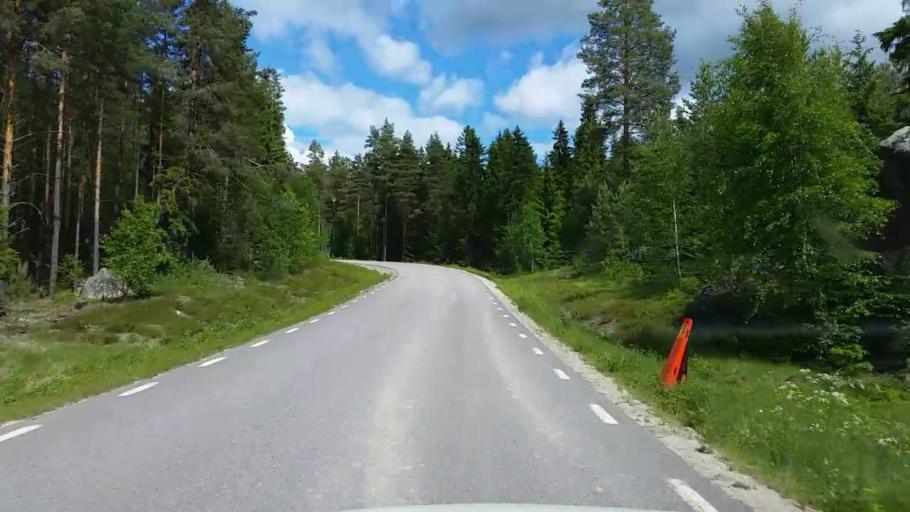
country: SE
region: Gaevleborg
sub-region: Ovanakers Kommun
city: Alfta
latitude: 61.4063
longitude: 16.0577
